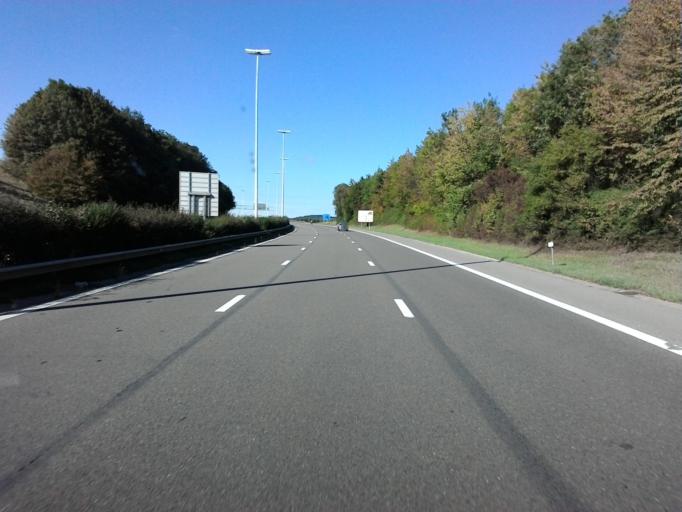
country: BE
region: Wallonia
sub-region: Province du Luxembourg
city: Aubange
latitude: 49.5683
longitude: 5.8214
